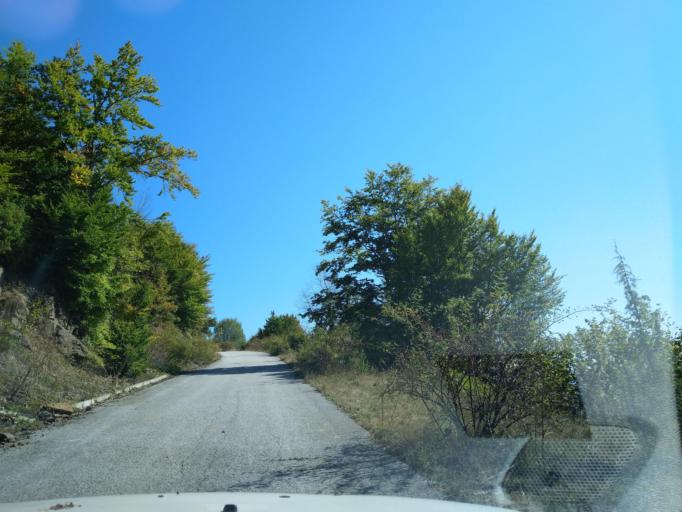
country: RS
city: Sokolovica
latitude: 43.2550
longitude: 20.3362
